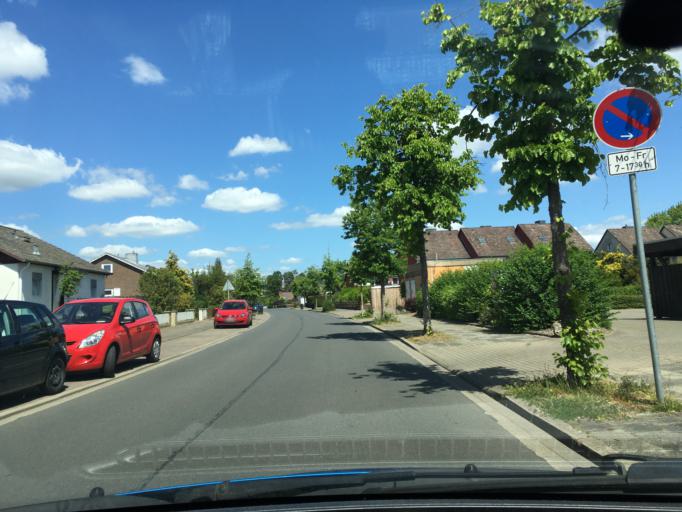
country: DE
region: Lower Saxony
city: Uelzen
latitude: 52.9669
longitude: 10.5321
